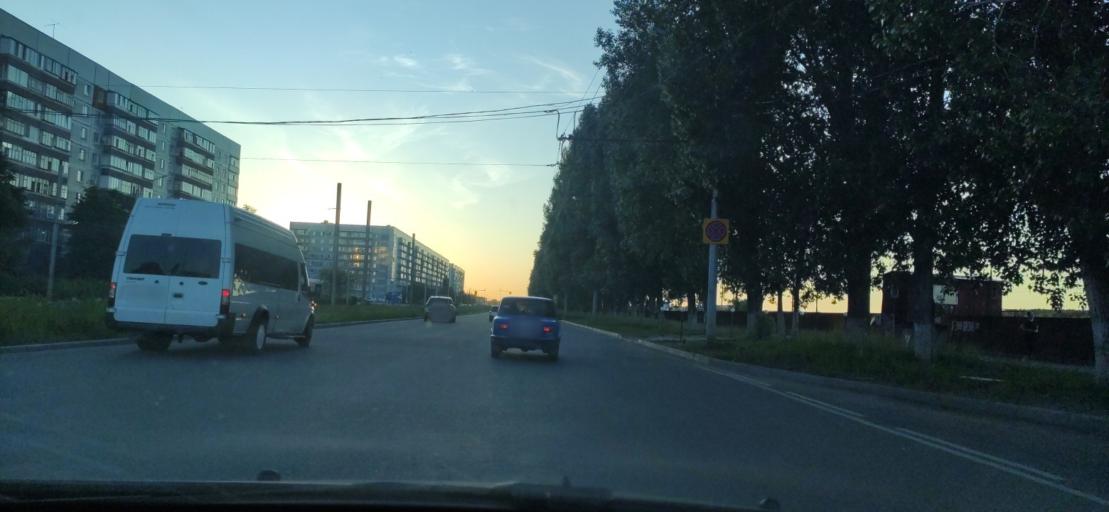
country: RU
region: Ulyanovsk
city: Mirnyy
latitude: 54.3828
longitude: 48.6198
